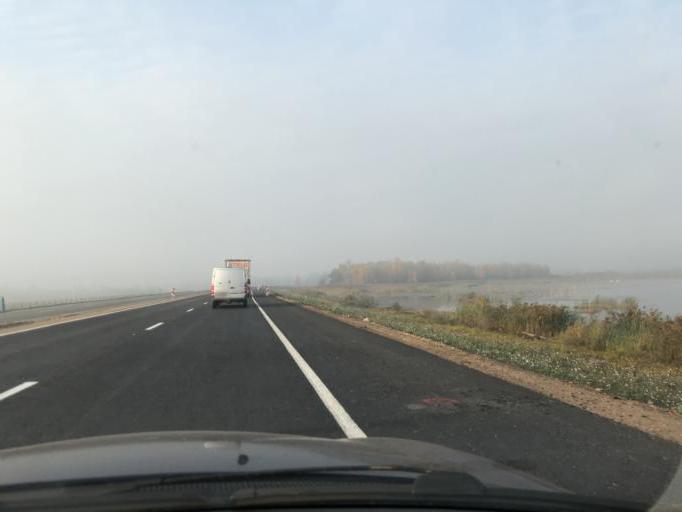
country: BY
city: Berezovka
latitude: 53.8343
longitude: 25.4622
